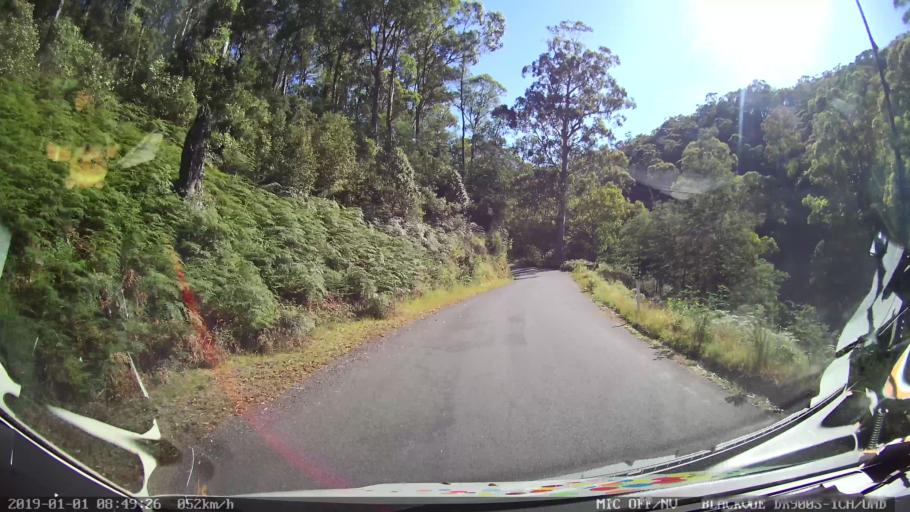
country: AU
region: New South Wales
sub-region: Snowy River
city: Jindabyne
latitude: -36.2823
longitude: 148.1999
